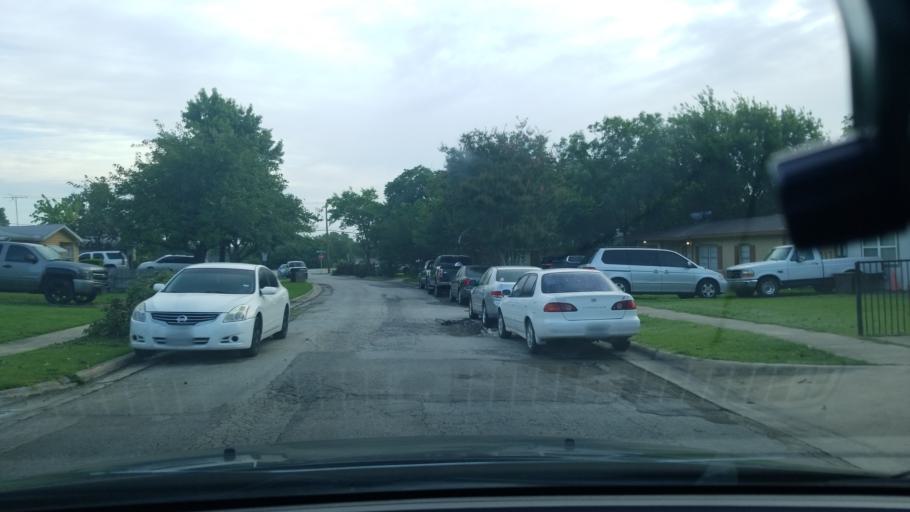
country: US
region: Texas
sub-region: Dallas County
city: Mesquite
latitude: 32.7671
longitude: -96.6377
